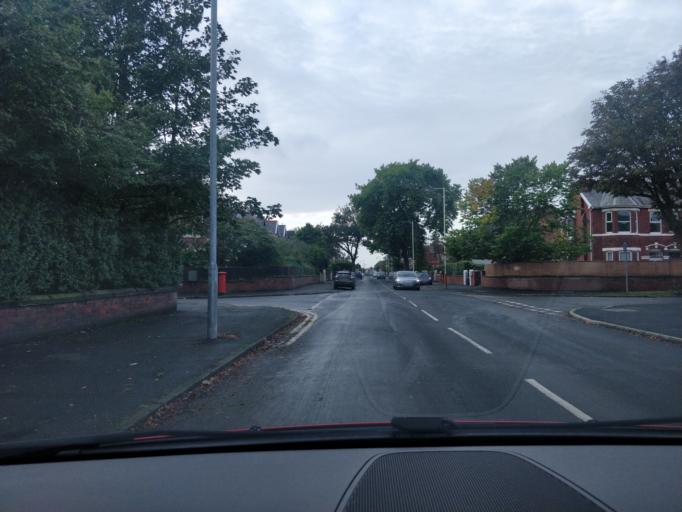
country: GB
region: England
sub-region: Sefton
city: Southport
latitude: 53.6407
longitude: -2.9831
